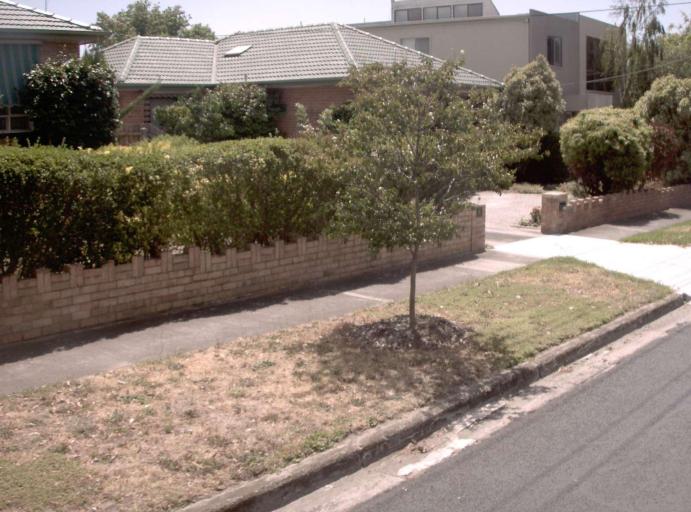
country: AU
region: Victoria
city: Highett
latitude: -37.9394
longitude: 145.0607
